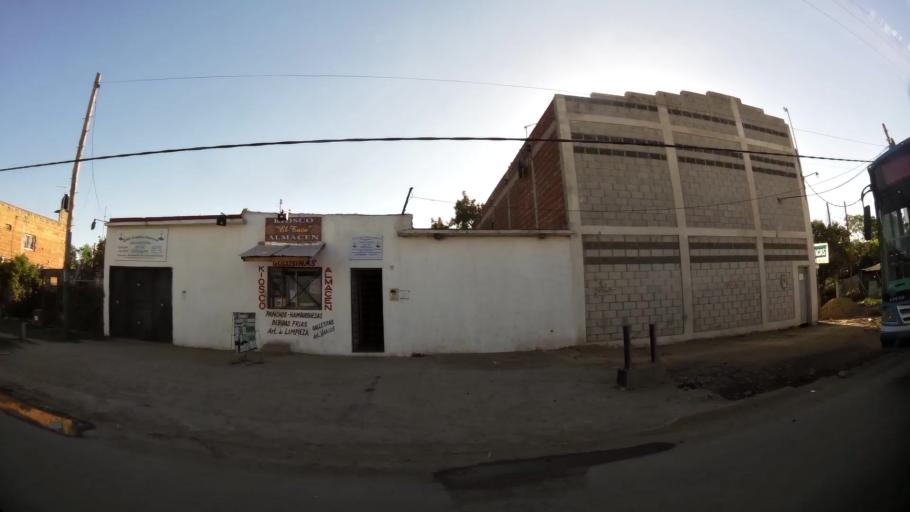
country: AR
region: Buenos Aires
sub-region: Partido de Almirante Brown
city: Adrogue
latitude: -34.7582
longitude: -58.3340
